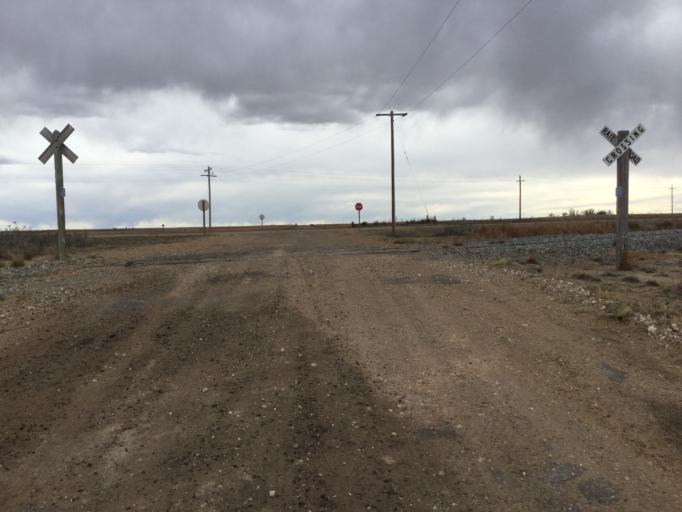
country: US
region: Kansas
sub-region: Morton County
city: Elkhart
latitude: 37.0486
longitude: -101.8270
